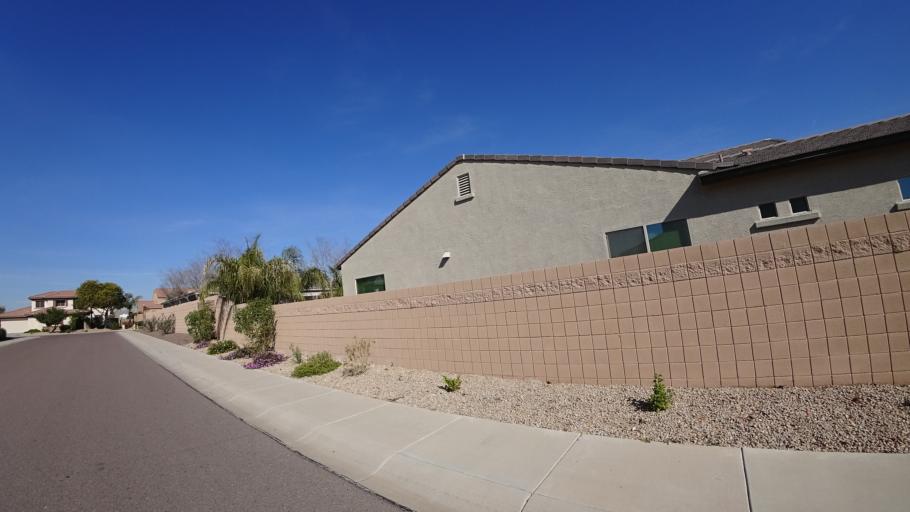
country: US
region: Arizona
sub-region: Maricopa County
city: Citrus Park
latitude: 33.5142
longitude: -112.4596
